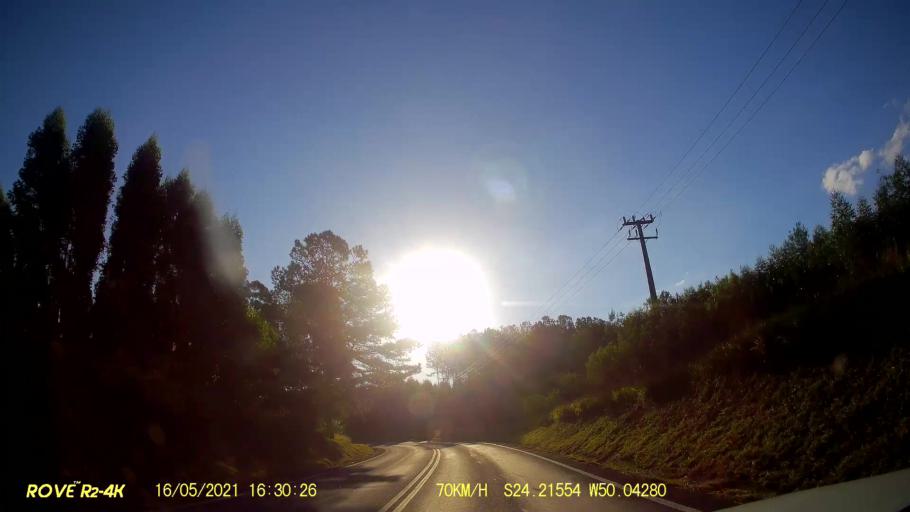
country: BR
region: Parana
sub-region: Pirai Do Sul
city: Pirai do Sul
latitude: -24.2155
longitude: -50.0431
